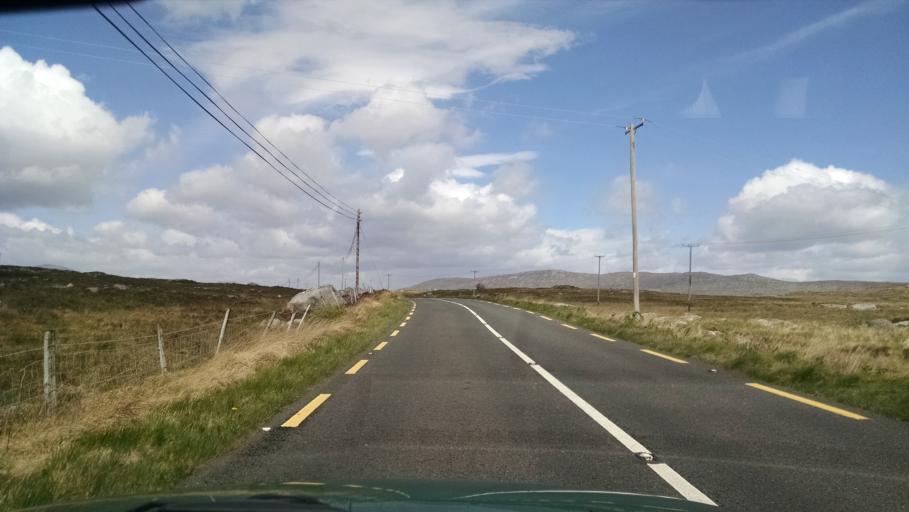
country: IE
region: Connaught
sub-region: County Galway
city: Oughterard
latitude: 53.3489
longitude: -9.5425
